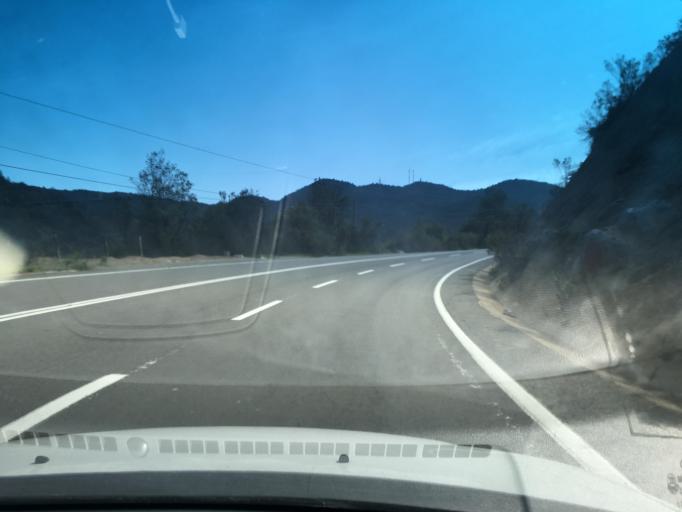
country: CL
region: Valparaiso
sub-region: Provincia de San Felipe
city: Llaillay
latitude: -33.0679
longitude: -70.9978
